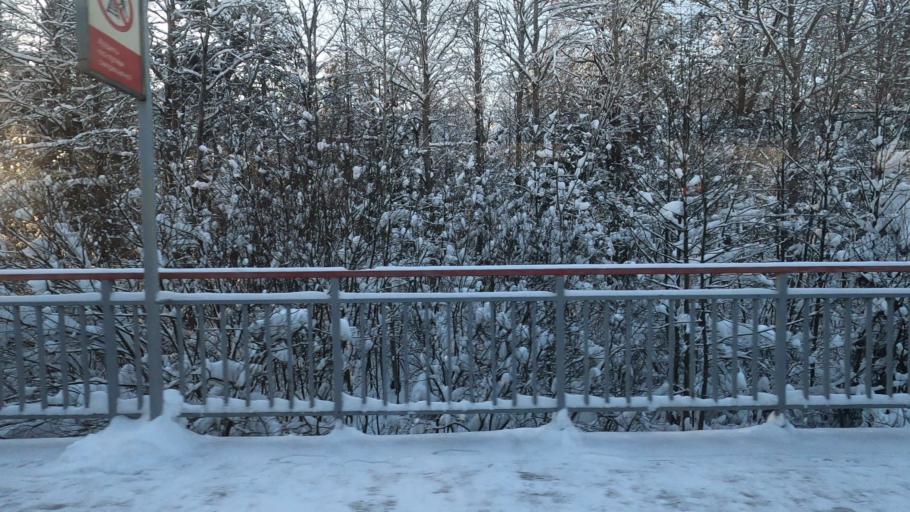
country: RU
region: Moskovskaya
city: Novo-Nikol'skoye
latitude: 56.6392
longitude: 37.5618
